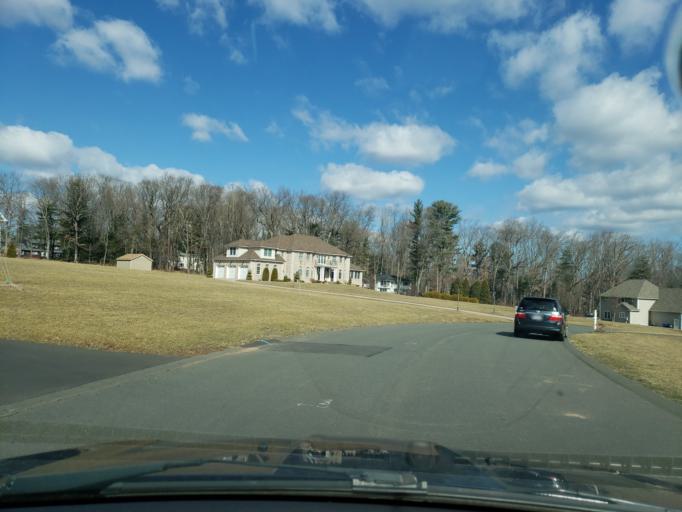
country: US
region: Connecticut
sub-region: Tolland County
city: Somers
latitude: 42.0068
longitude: -72.4823
